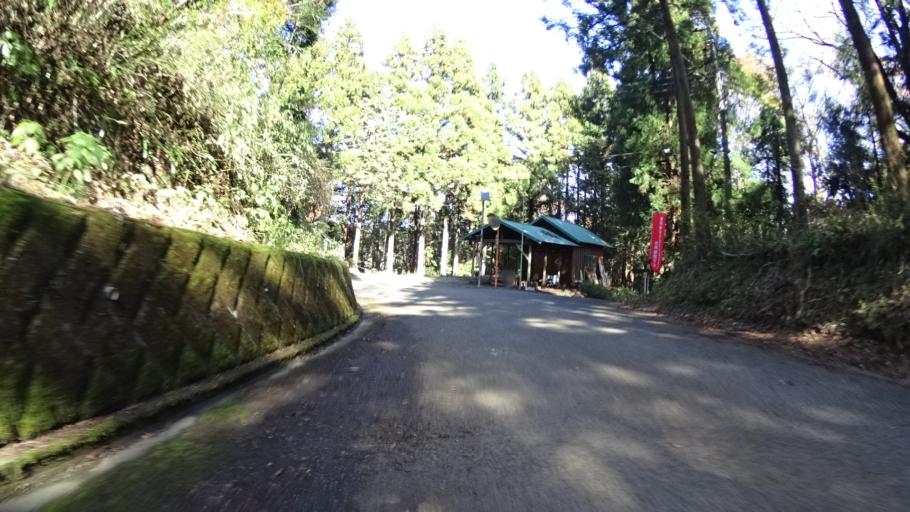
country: JP
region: Kanagawa
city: Zama
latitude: 35.5272
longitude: 139.2730
